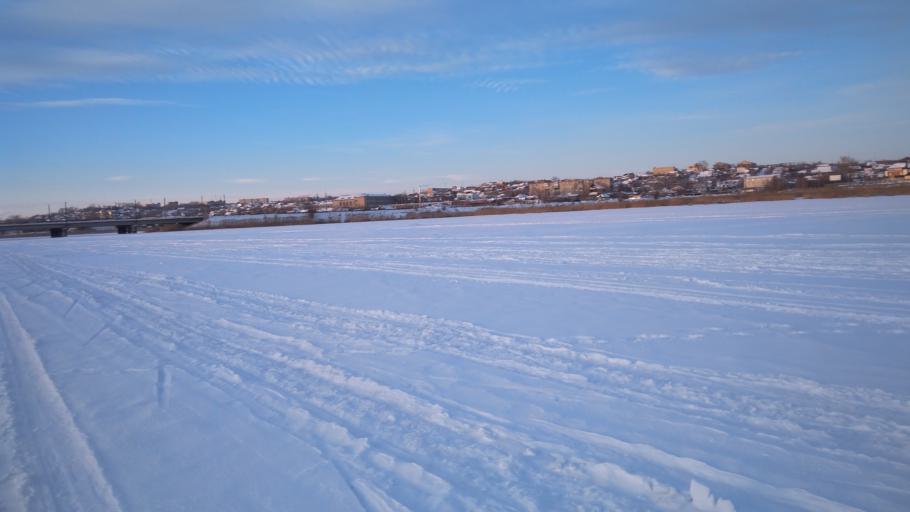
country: RU
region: Chelyabinsk
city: Troitsk
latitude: 54.0896
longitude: 61.5793
